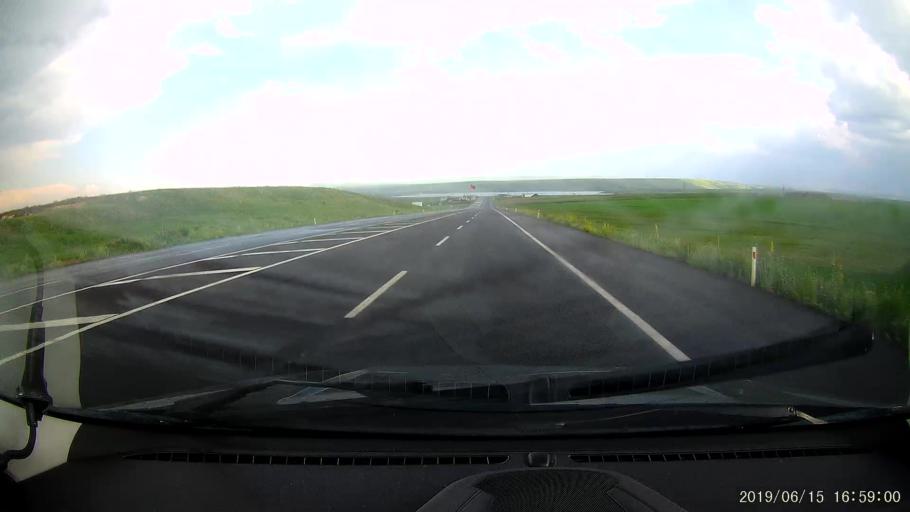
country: TR
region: Kars
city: Susuz
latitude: 40.7578
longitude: 43.1472
